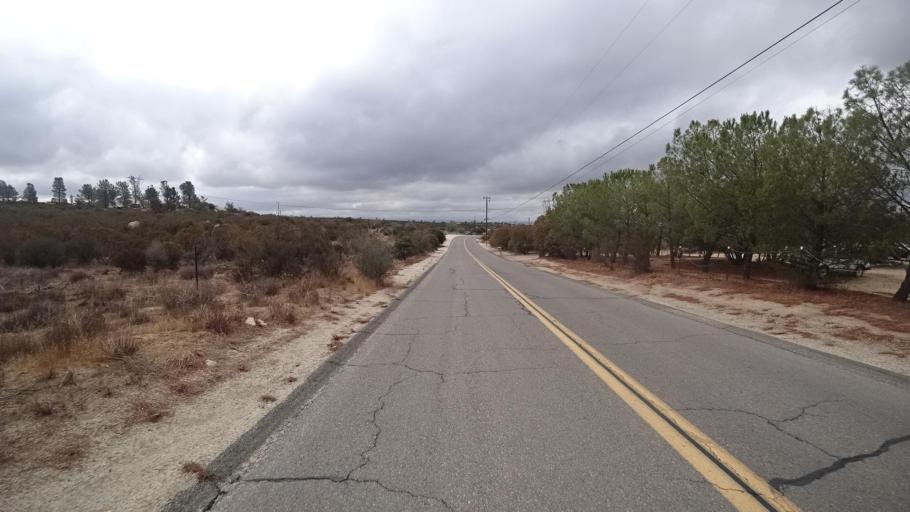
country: US
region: California
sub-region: San Diego County
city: Campo
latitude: 32.6075
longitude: -116.3338
